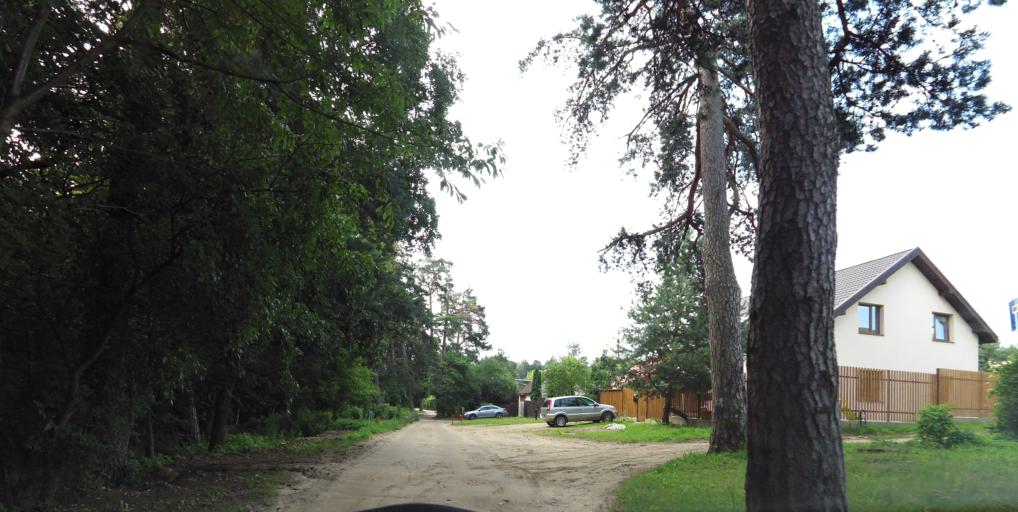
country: LT
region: Vilnius County
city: Seskine
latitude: 54.7349
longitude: 25.2844
